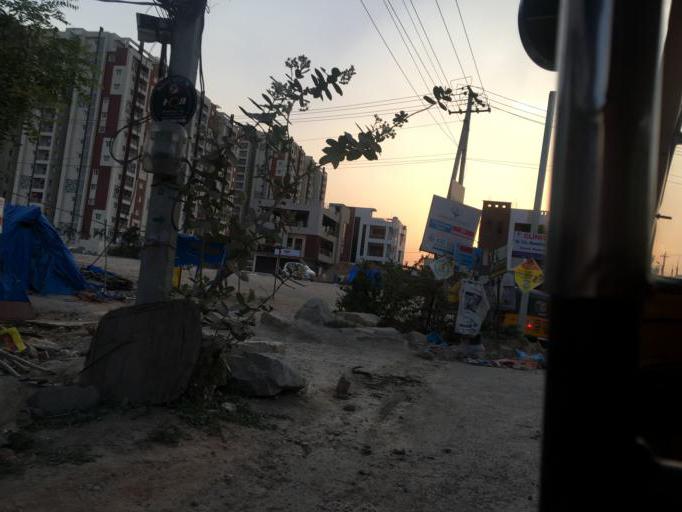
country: IN
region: Telangana
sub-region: Medak
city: Serilingampalle
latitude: 17.4356
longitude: 78.3345
